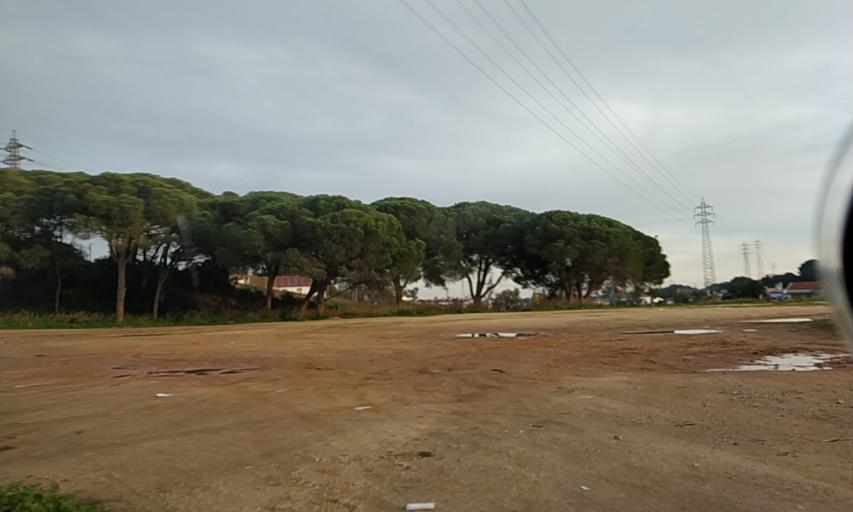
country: PT
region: Setubal
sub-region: Setubal
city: Setubal
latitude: 38.5260
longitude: -8.8586
